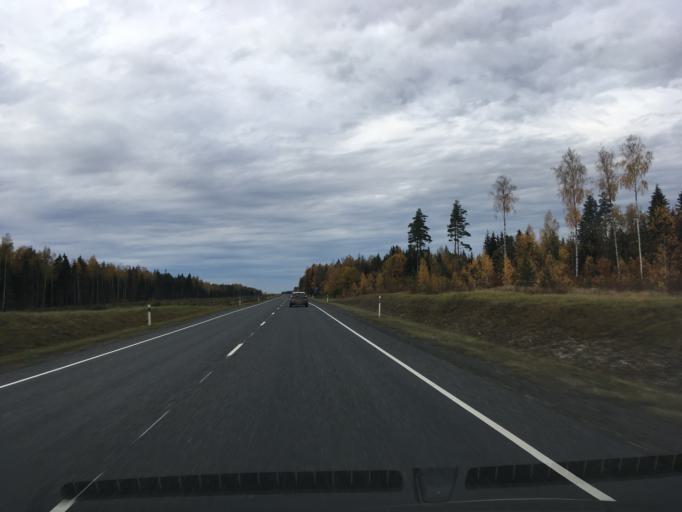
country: EE
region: Harju
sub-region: Nissi vald
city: Turba
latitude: 58.9528
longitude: 24.0806
